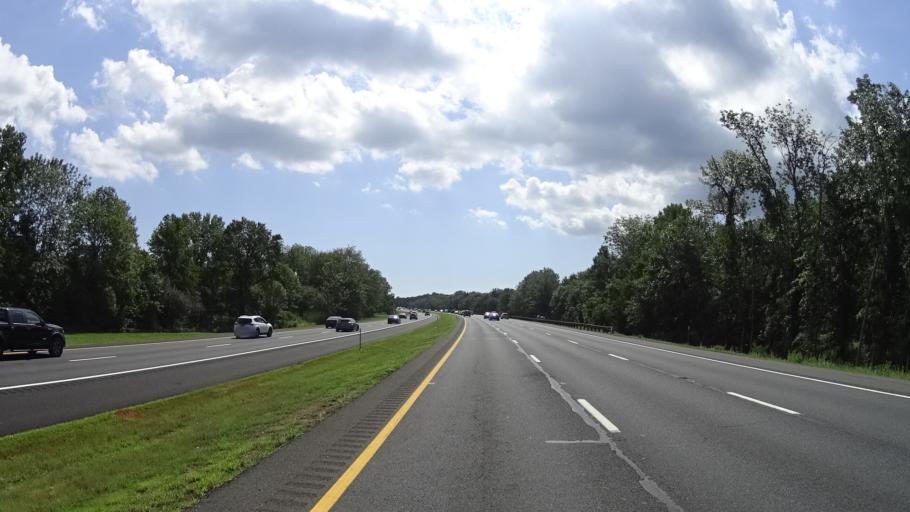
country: US
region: New Jersey
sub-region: Monmouth County
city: Lincroft
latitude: 40.3604
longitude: -74.1361
